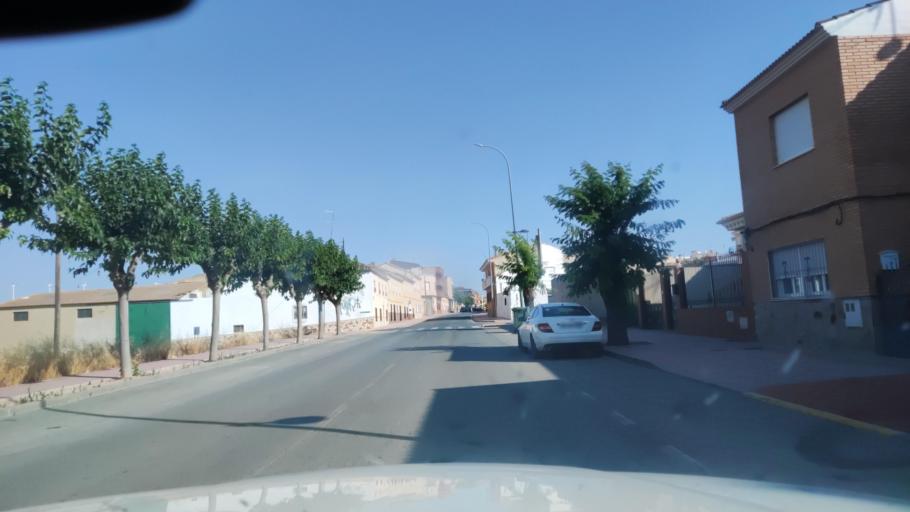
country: ES
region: Castille-La Mancha
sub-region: Provincia de Albacete
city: Pozo-Canada
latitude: 38.8061
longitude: -1.7345
